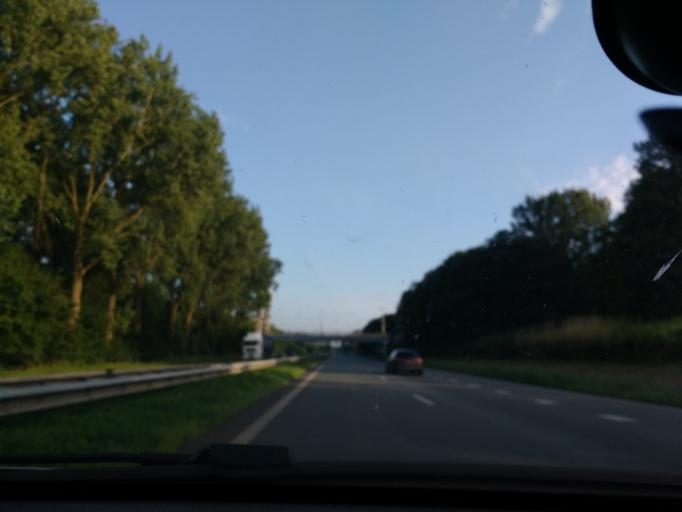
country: NL
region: Gelderland
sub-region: Gemeente Arnhem
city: Burgemeesterswijk
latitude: 51.9478
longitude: 5.8788
